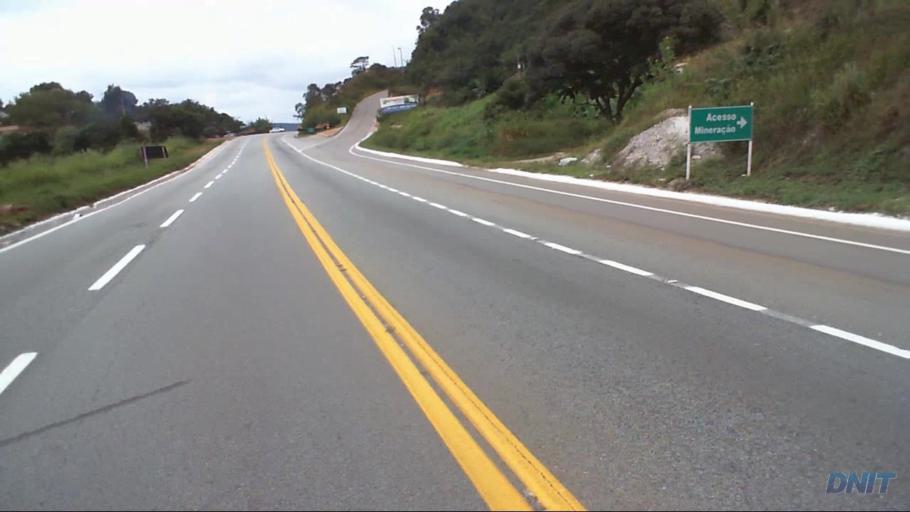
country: BR
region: Minas Gerais
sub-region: Caete
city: Caete
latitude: -19.7865
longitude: -43.6885
